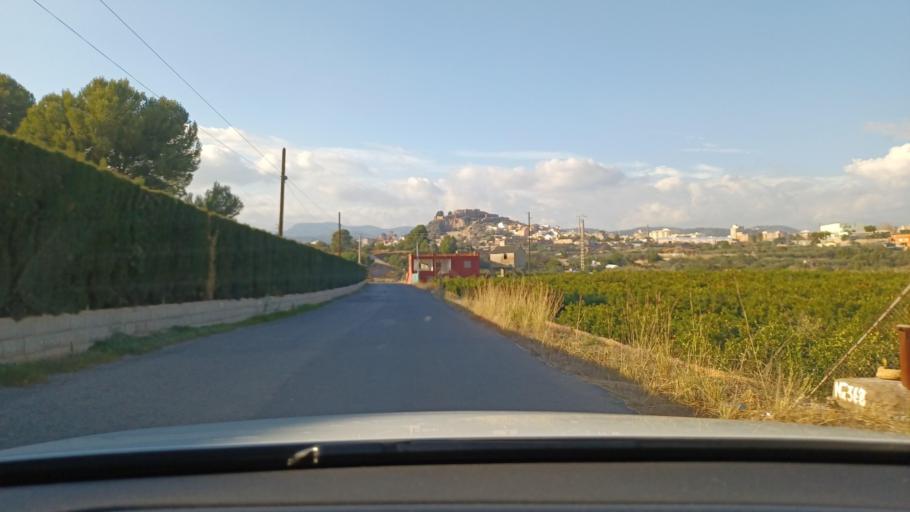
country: ES
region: Valencia
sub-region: Provincia de Castello
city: Onda
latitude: 39.9569
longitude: -0.2473
